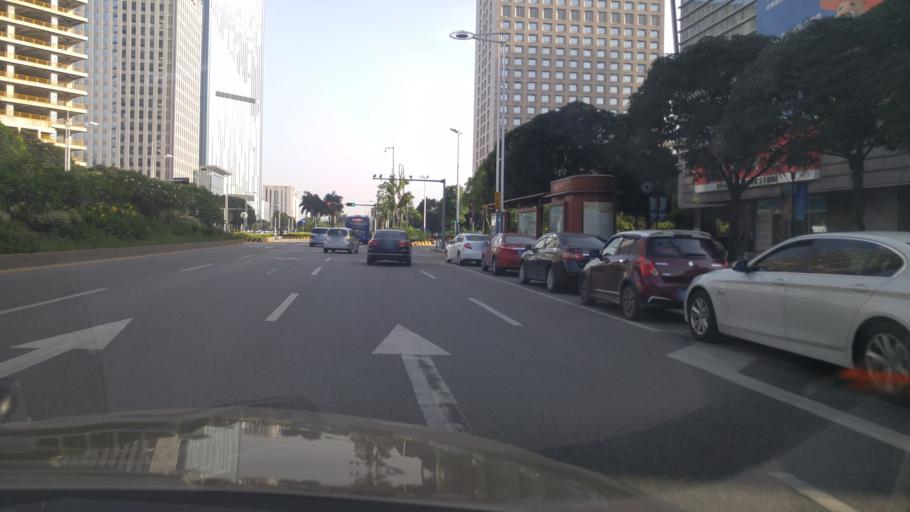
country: CN
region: Guangdong
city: Foshan
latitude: 23.0618
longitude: 113.1433
